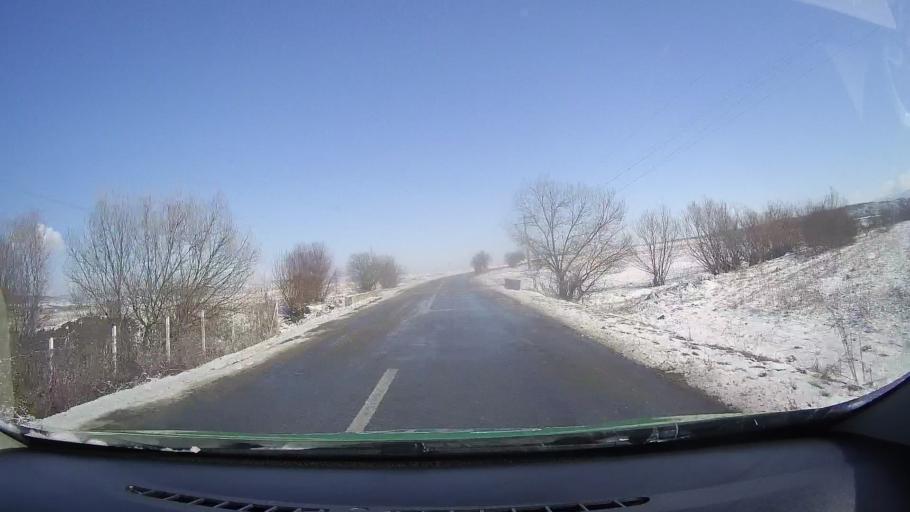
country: RO
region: Sibiu
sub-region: Comuna Racovita
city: Racovita
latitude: 45.6740
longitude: 24.3252
